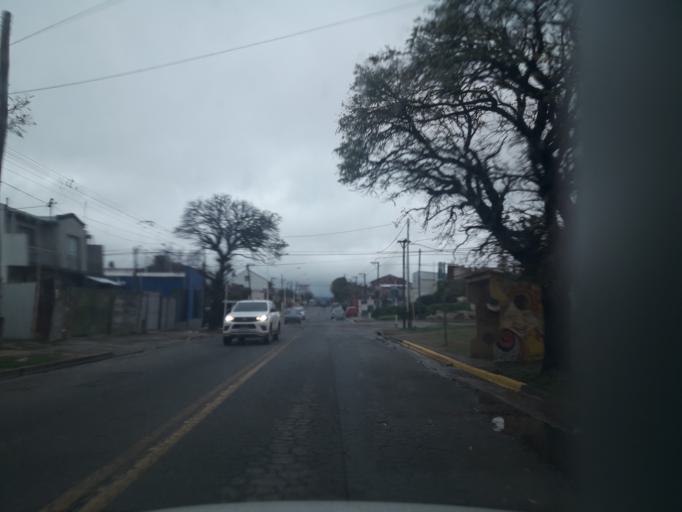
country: AR
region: Buenos Aires
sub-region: Partido de Tandil
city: Tandil
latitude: -37.3117
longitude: -59.1558
